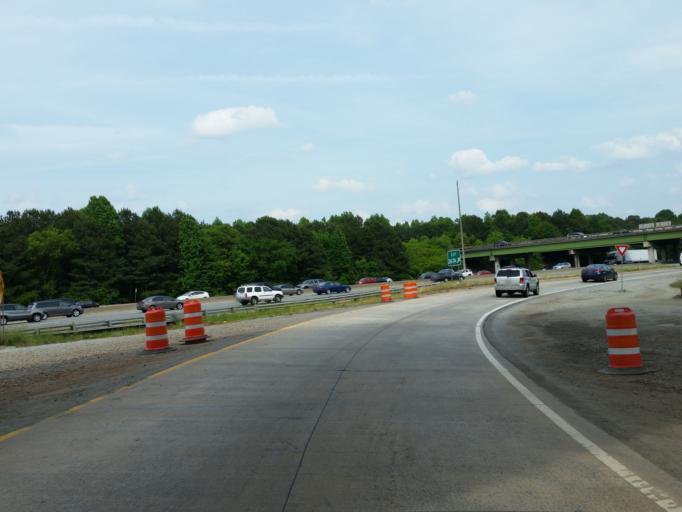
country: US
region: Georgia
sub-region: Cobb County
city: Marietta
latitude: 33.9852
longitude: -84.5438
